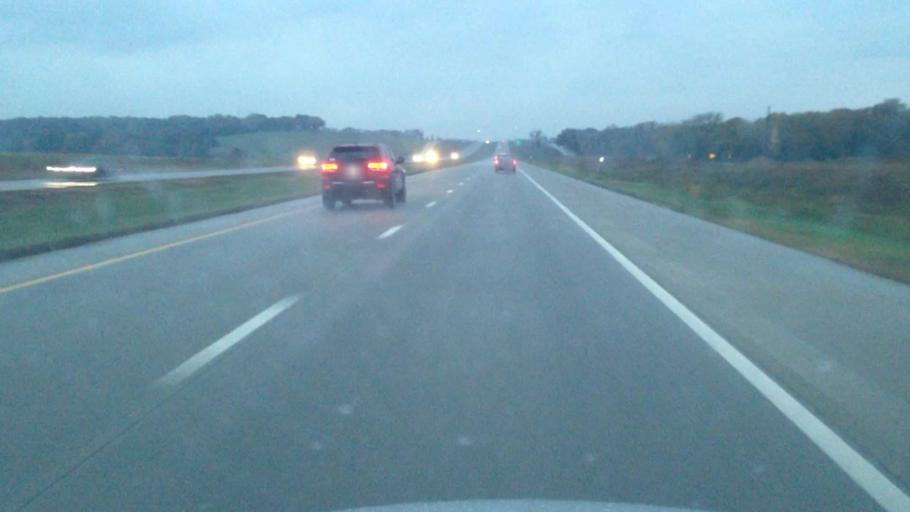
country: US
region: Kansas
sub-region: Douglas County
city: Baldwin City
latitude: 38.8036
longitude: -95.2692
